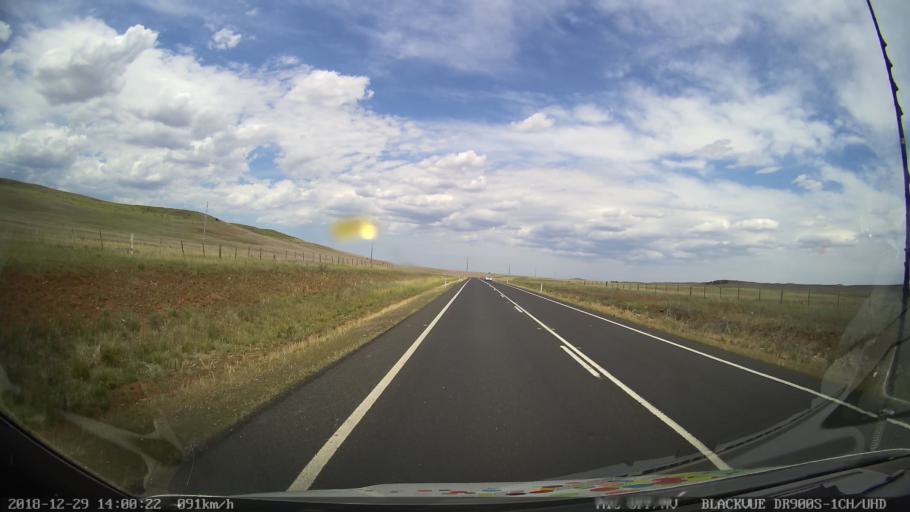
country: AU
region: New South Wales
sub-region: Cooma-Monaro
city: Cooma
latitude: -36.2632
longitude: 149.1577
